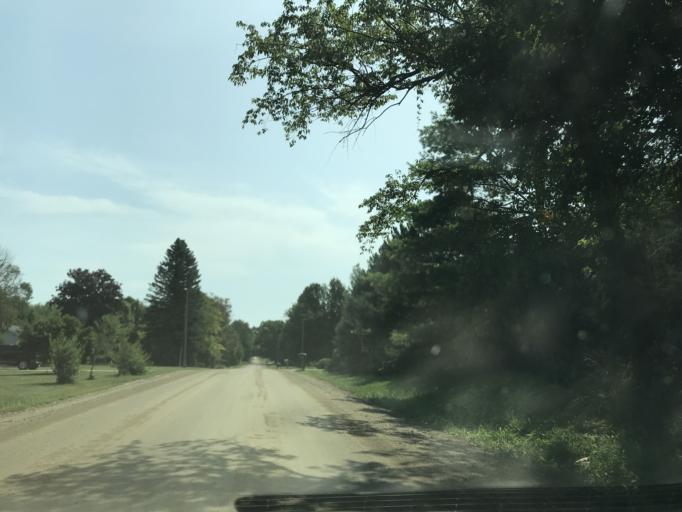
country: US
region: Michigan
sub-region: Eaton County
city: Grand Ledge
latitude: 42.7699
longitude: -84.7000
